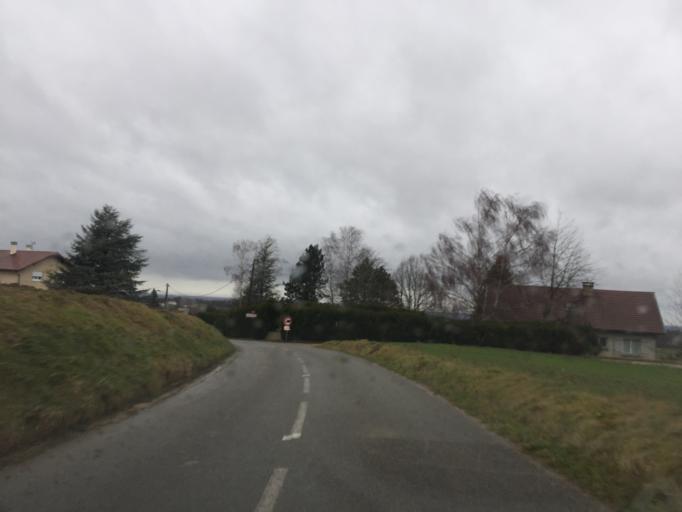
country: FR
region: Franche-Comte
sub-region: Departement du Jura
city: Dole
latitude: 47.1598
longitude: 5.5021
